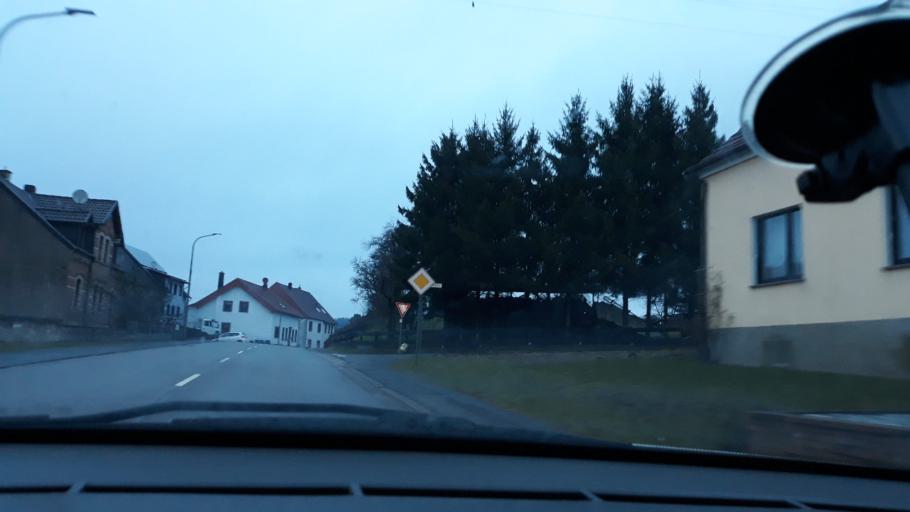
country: DE
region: Saarland
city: Blieskastel
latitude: 49.1936
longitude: 7.2490
